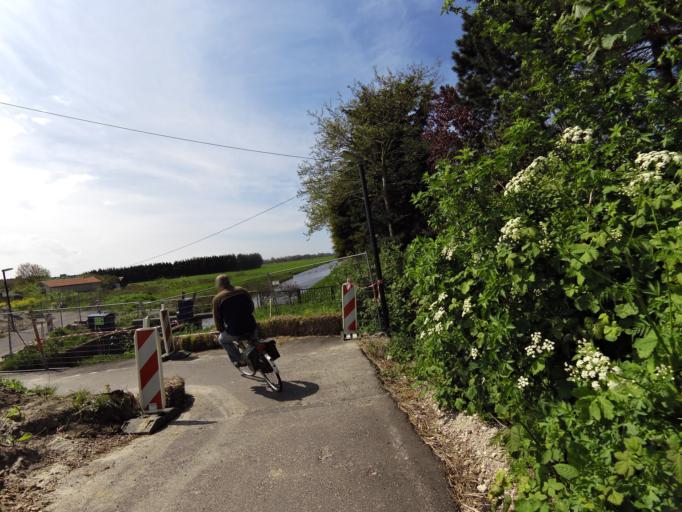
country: NL
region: South Holland
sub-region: Gemeente Hellevoetsluis
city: Nieuwenhoorn
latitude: 51.8463
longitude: 4.1396
